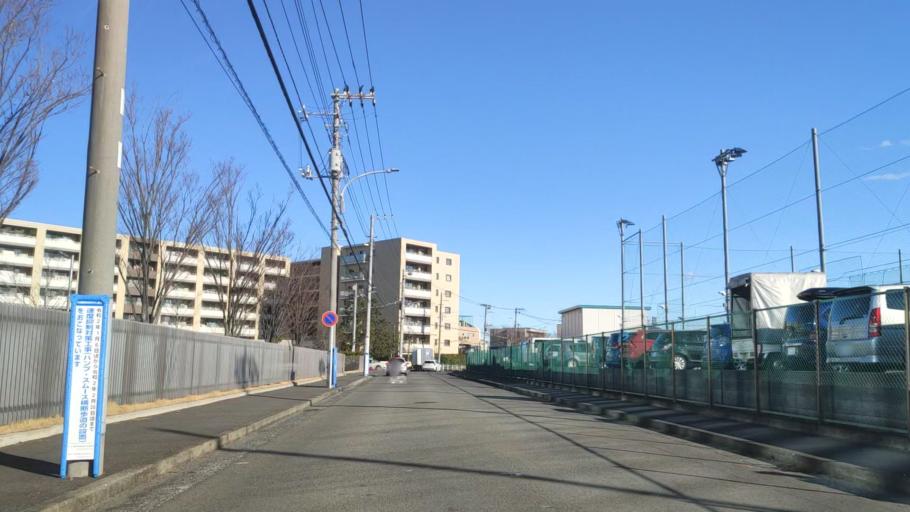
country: JP
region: Tokyo
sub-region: Machida-shi
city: Machida
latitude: 35.5158
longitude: 139.5444
